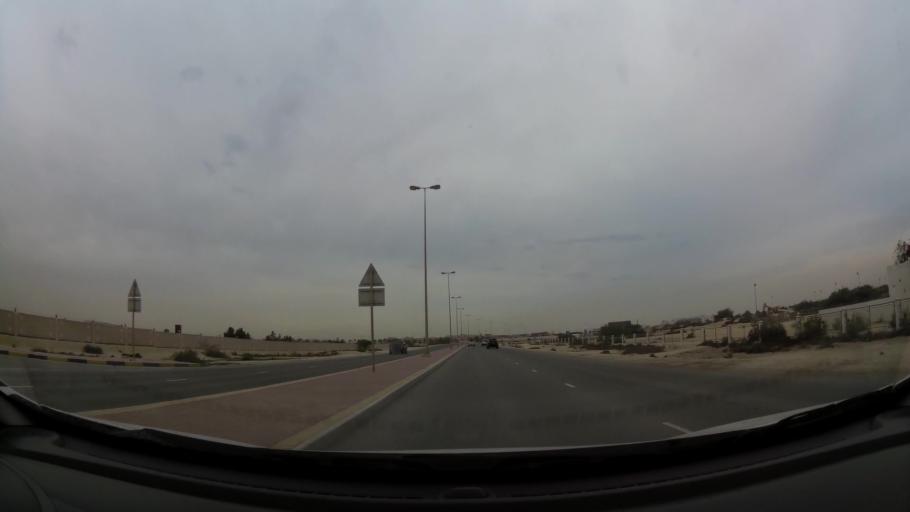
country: BH
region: Northern
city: Ar Rifa'
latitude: 26.0969
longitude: 50.5566
